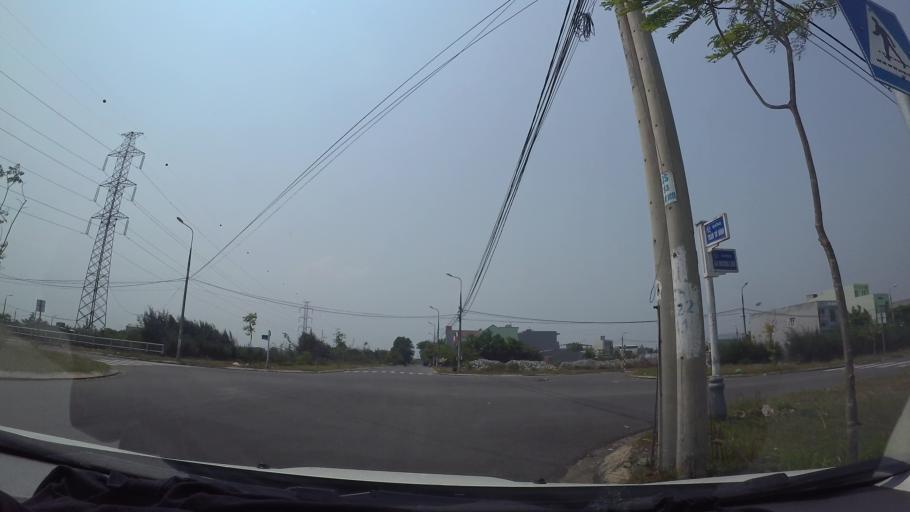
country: VN
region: Da Nang
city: Cam Le
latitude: 15.9942
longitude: 108.2003
